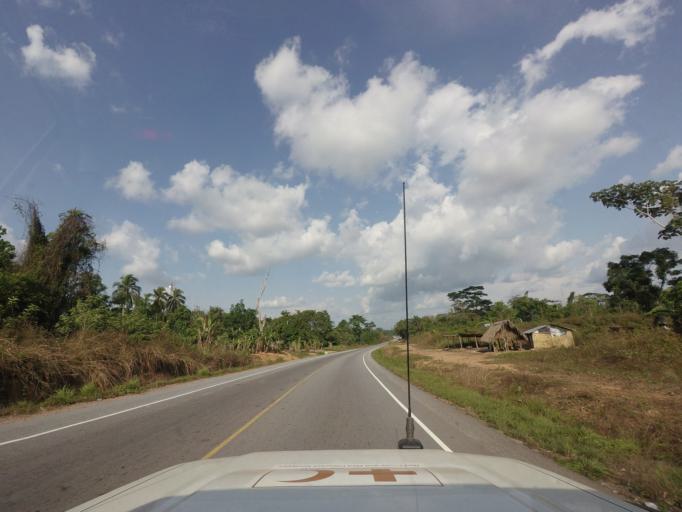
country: LR
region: Bong
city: Gbarnga
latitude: 6.8898
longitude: -9.6905
